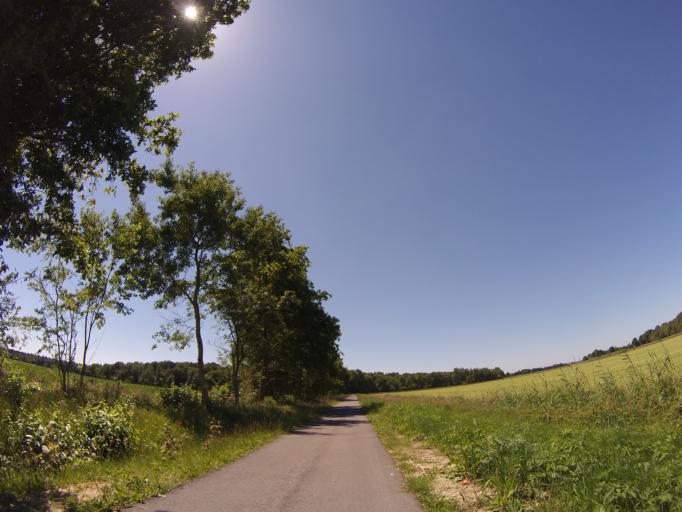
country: NL
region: Drenthe
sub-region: Gemeente Assen
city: Assen
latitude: 52.9373
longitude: 6.5733
